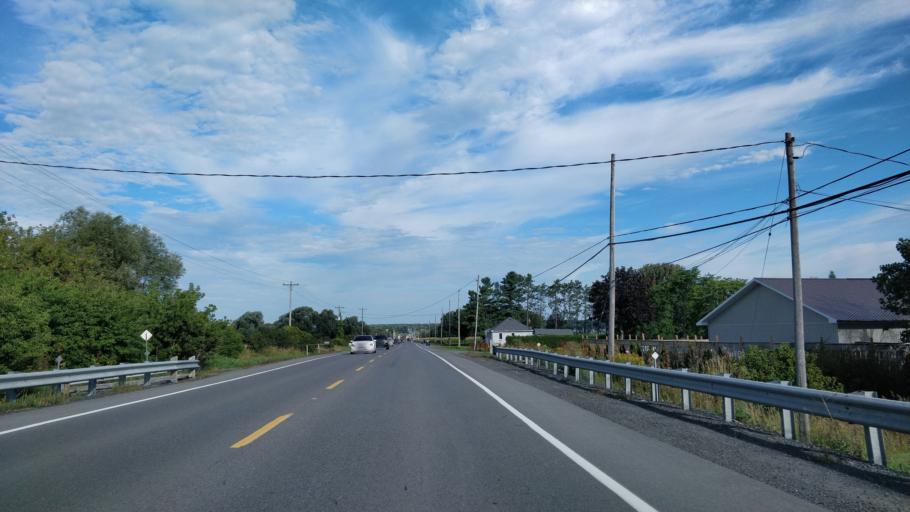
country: CA
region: Ontario
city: Bells Corners
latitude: 45.3288
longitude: -76.0162
